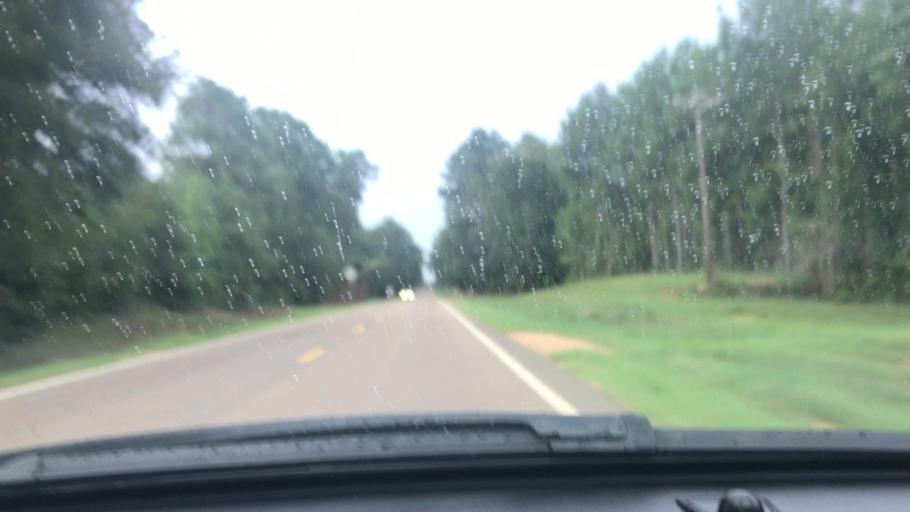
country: US
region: Mississippi
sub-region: Pike County
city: Summit
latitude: 31.3502
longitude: -90.6011
